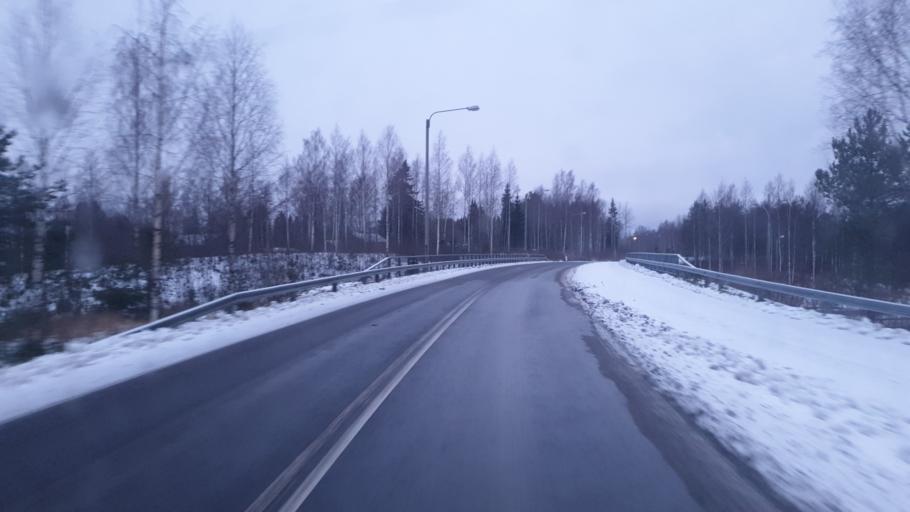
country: FI
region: Northern Savo
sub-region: Kuopio
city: Siilinjaervi
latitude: 63.0586
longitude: 27.6729
